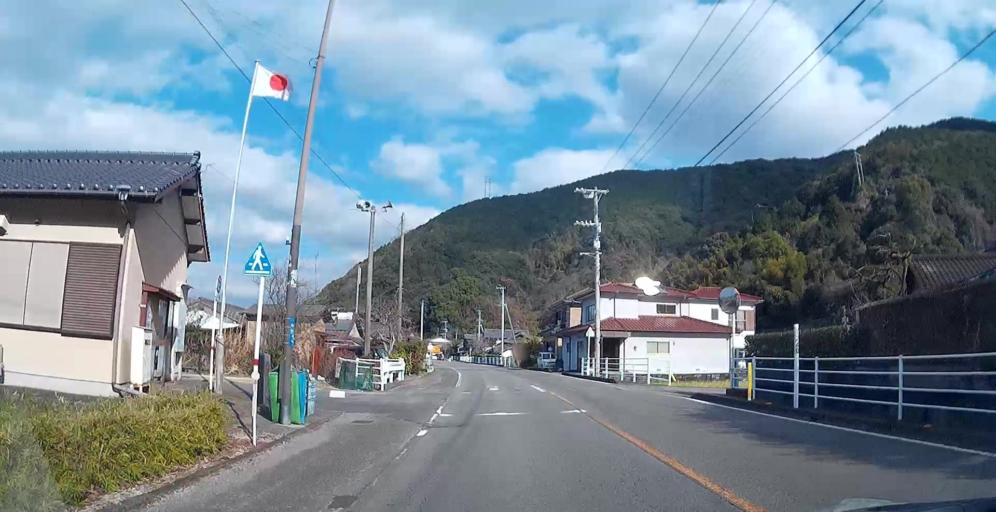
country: JP
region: Kumamoto
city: Yatsushiro
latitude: 32.4224
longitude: 130.5549
